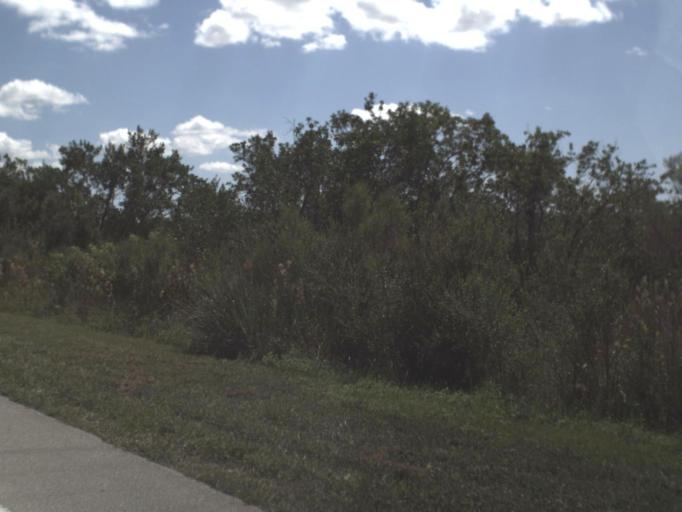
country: US
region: Florida
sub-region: Collier County
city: Lely Resort
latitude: 25.9853
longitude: -81.5676
